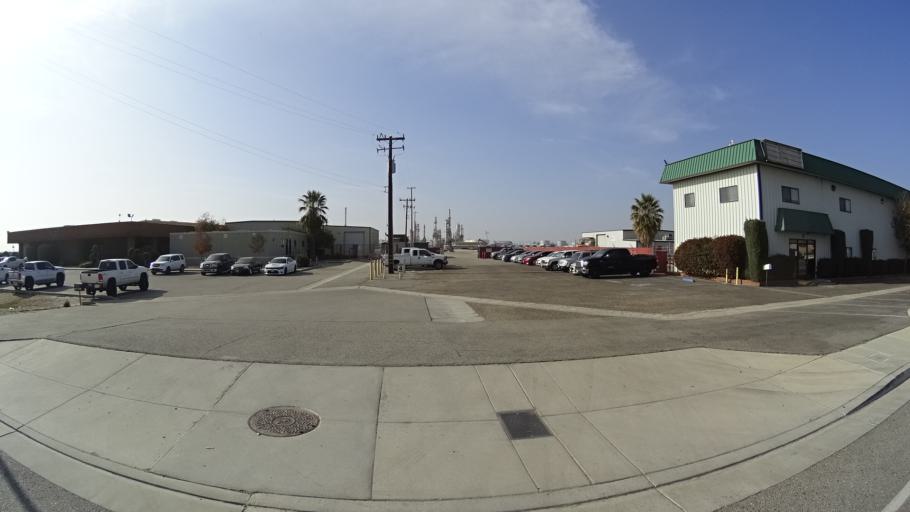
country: US
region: California
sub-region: Kern County
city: Greenacres
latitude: 35.3797
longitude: -119.0657
